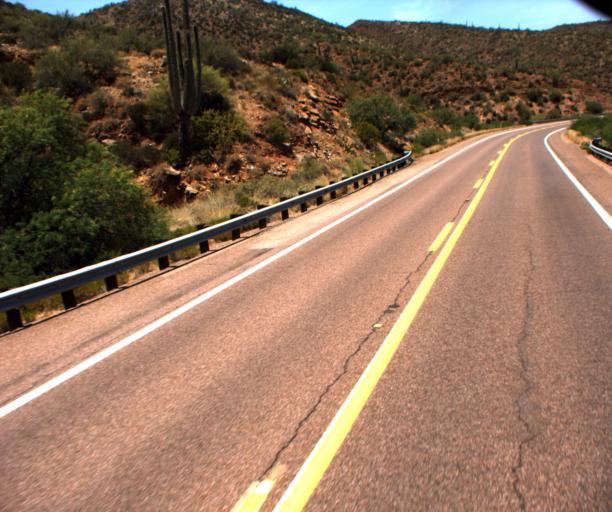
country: US
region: Arizona
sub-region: Gila County
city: Tonto Basin
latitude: 33.6835
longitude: -111.1702
